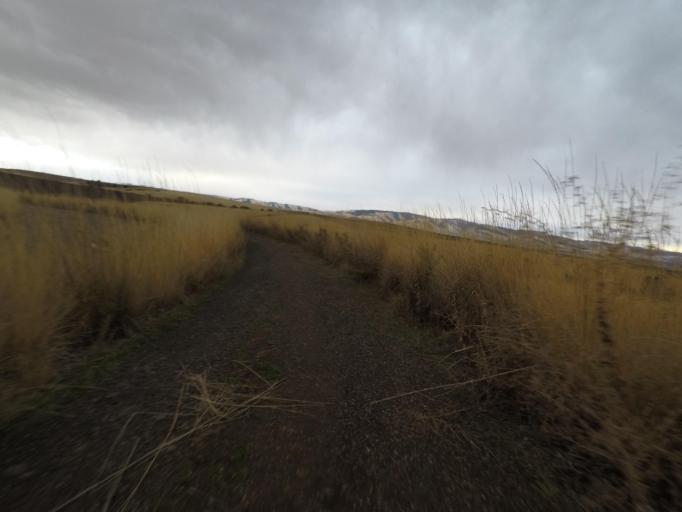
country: US
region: Washington
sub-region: Walla Walla County
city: Walla Walla East
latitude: 46.0626
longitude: -118.2677
